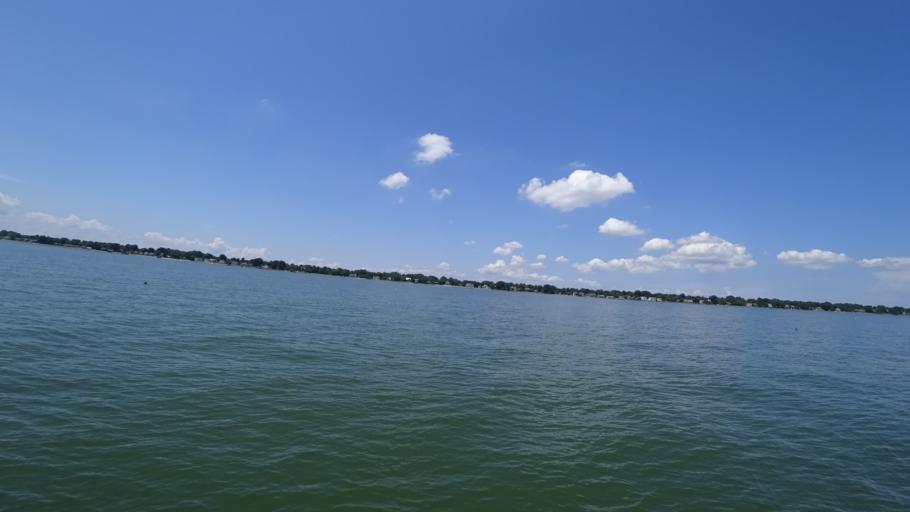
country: US
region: Virginia
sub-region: City of Hampton
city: Hampton
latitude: 36.9899
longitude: -76.3714
